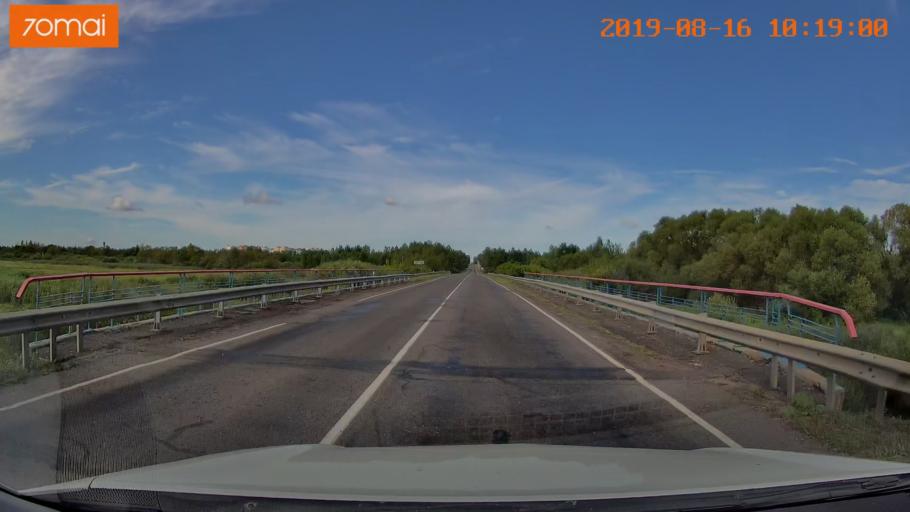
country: BY
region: Mogilev
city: Asipovichy
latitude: 53.3061
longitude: 28.6767
